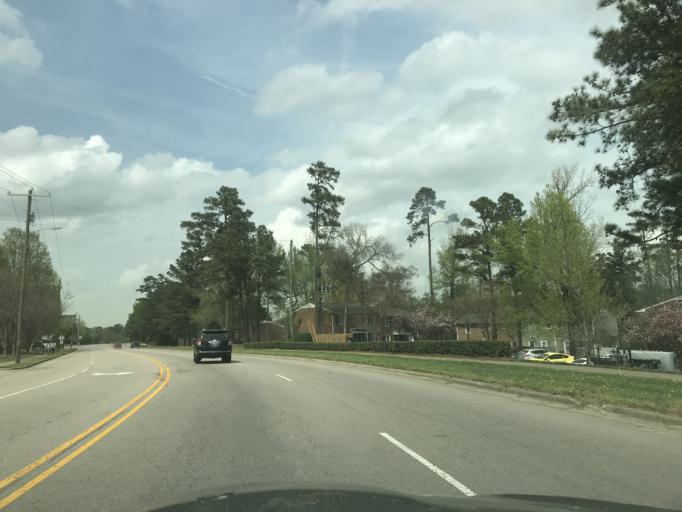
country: US
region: North Carolina
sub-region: Wake County
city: Raleigh
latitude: 35.8066
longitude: -78.5946
